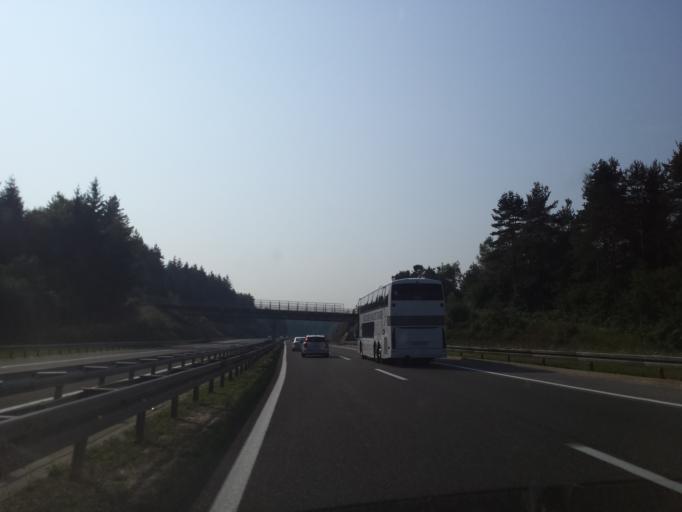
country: HR
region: Karlovacka
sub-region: Grad Ogulin
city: Ogulin
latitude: 45.3824
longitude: 15.2631
